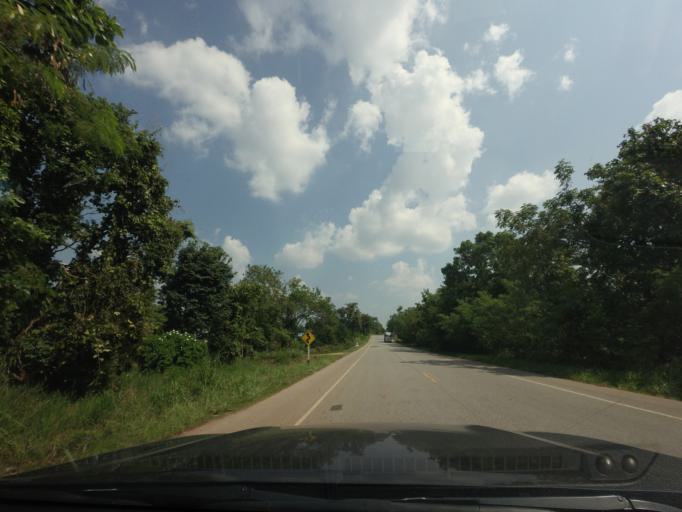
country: TH
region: Phitsanulok
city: Chat Trakan
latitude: 17.2626
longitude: 100.5544
